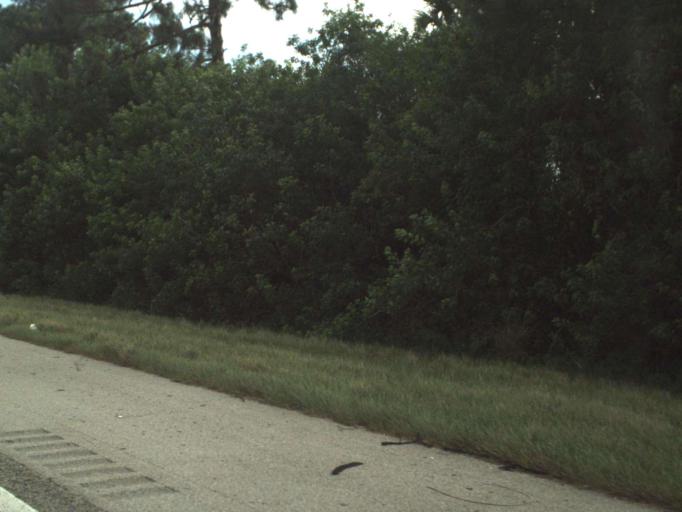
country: US
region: Florida
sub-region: Saint Lucie County
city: River Park
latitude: 27.3457
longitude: -80.4139
